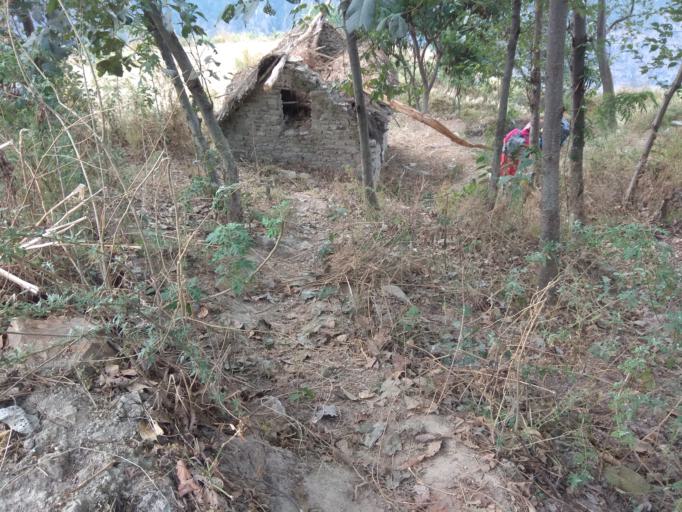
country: NP
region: Far Western
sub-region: Seti Zone
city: Achham
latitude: 29.2322
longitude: 81.6435
